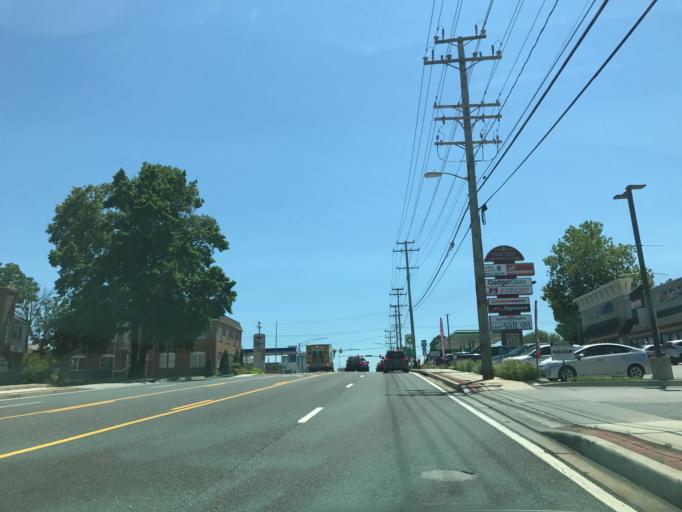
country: US
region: Maryland
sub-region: Baltimore County
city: Lutherville
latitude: 39.4217
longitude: -76.6174
